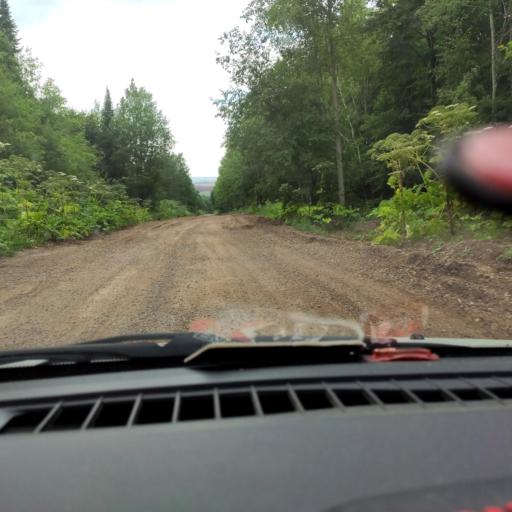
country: RU
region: Perm
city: Kultayevo
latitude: 57.8153
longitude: 56.0010
